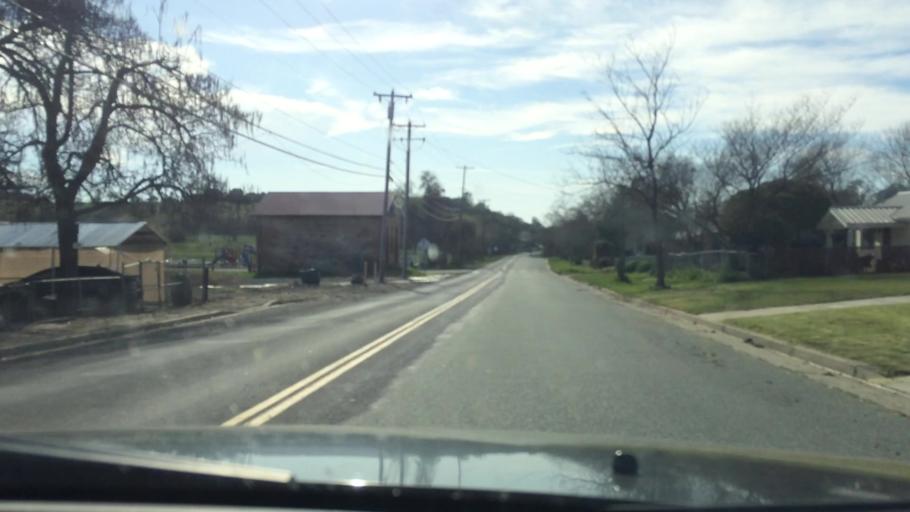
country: US
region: California
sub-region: Amador County
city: Plymouth
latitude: 38.4806
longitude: -120.8518
